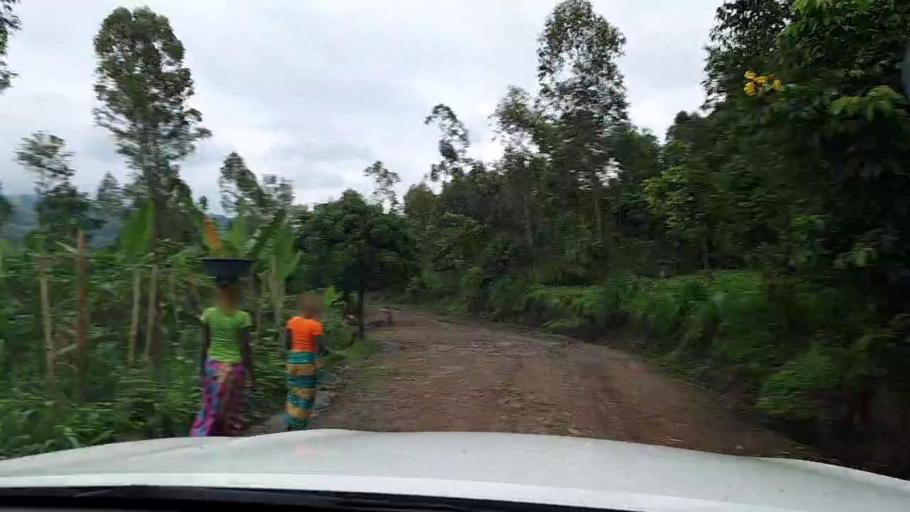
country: RW
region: Western Province
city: Cyangugu
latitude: -2.5494
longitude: 29.0383
